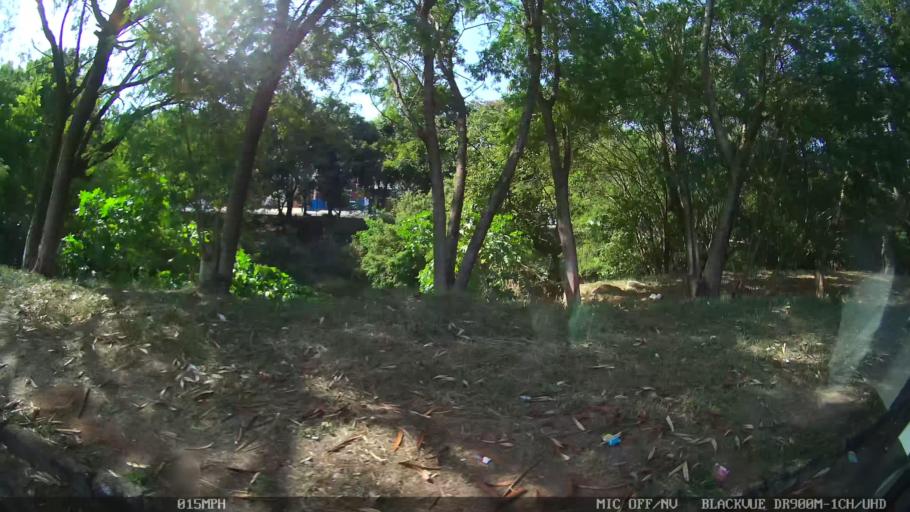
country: BR
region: Sao Paulo
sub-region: Sao Jose Do Rio Preto
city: Sao Jose do Rio Preto
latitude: -20.7933
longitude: -49.4048
